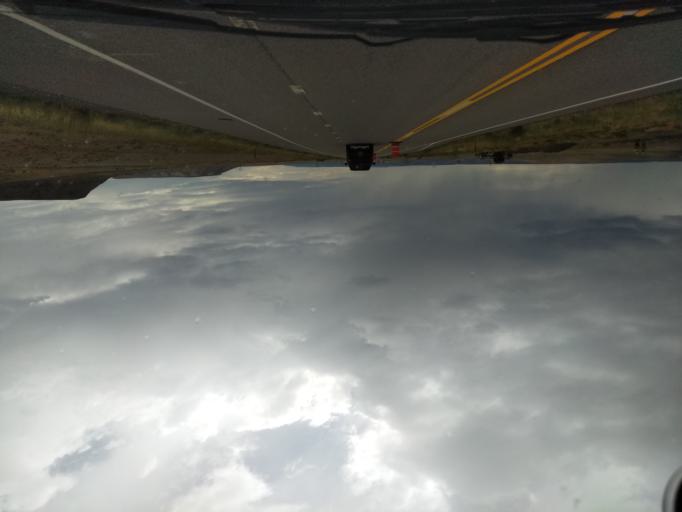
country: US
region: Colorado
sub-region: Delta County
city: Delta
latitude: 38.7559
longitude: -108.1761
